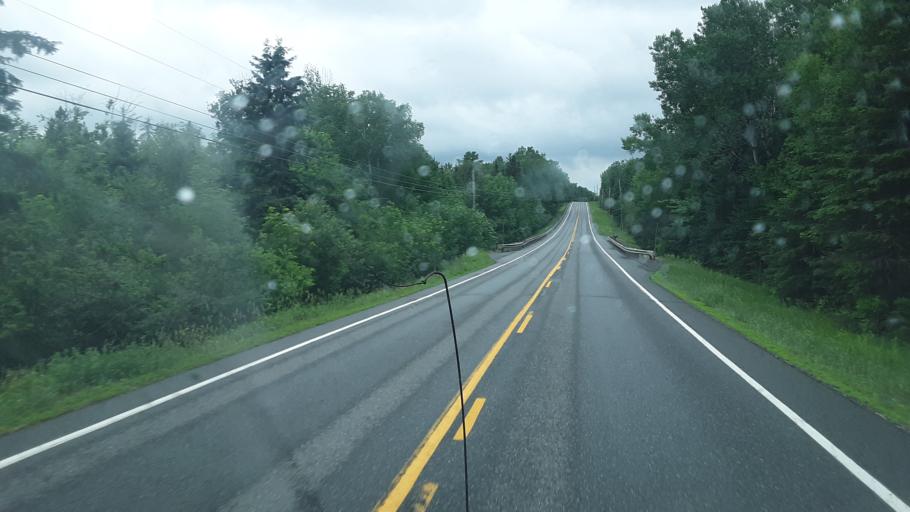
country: US
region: Maine
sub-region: Aroostook County
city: Presque Isle
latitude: 46.4624
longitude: -68.3870
